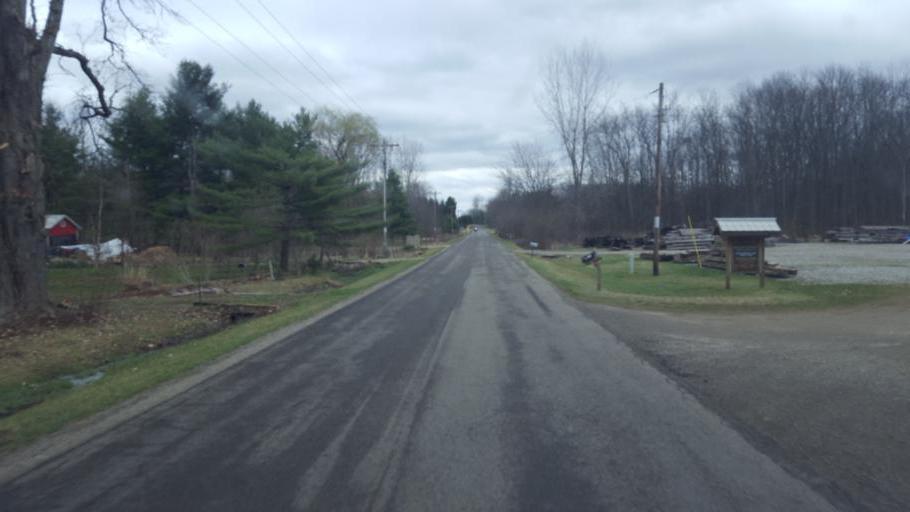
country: US
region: Ohio
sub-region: Knox County
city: Fredericktown
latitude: 40.4267
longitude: -82.6456
